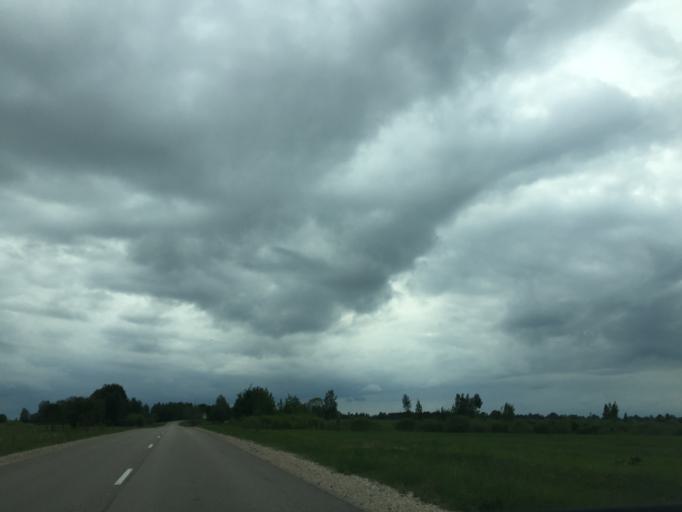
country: LV
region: Preilu Rajons
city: Preili
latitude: 56.0754
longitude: 26.7158
